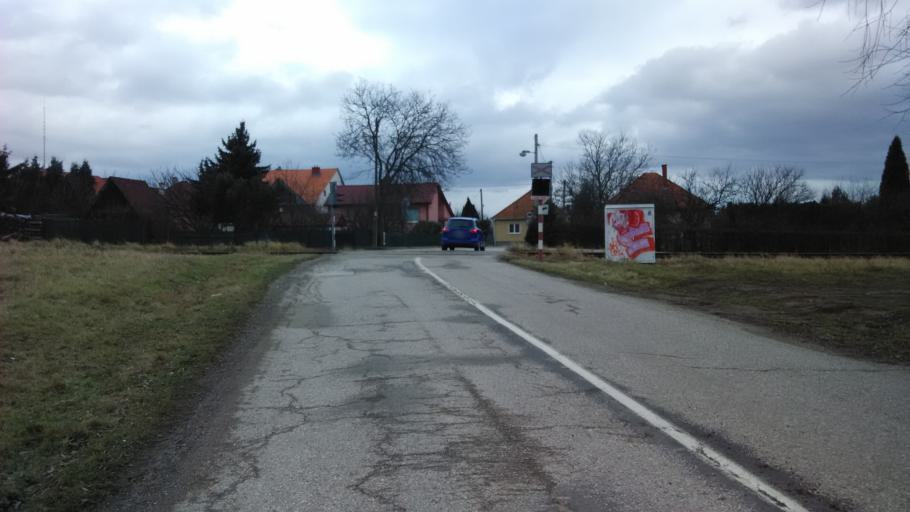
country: SK
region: Nitriansky
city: Zlate Moravce
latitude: 48.3905
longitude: 18.4080
